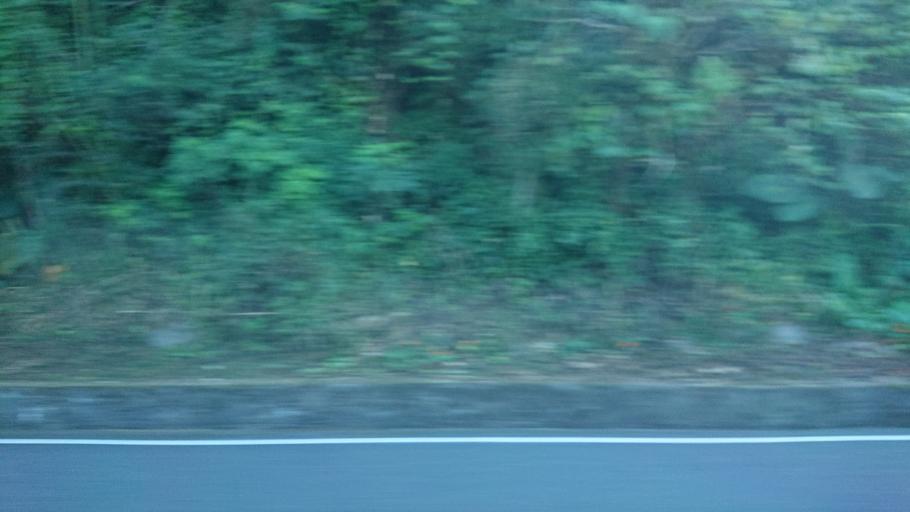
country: TW
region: Taiwan
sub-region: Chiayi
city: Jiayi Shi
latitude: 23.4718
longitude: 120.7182
